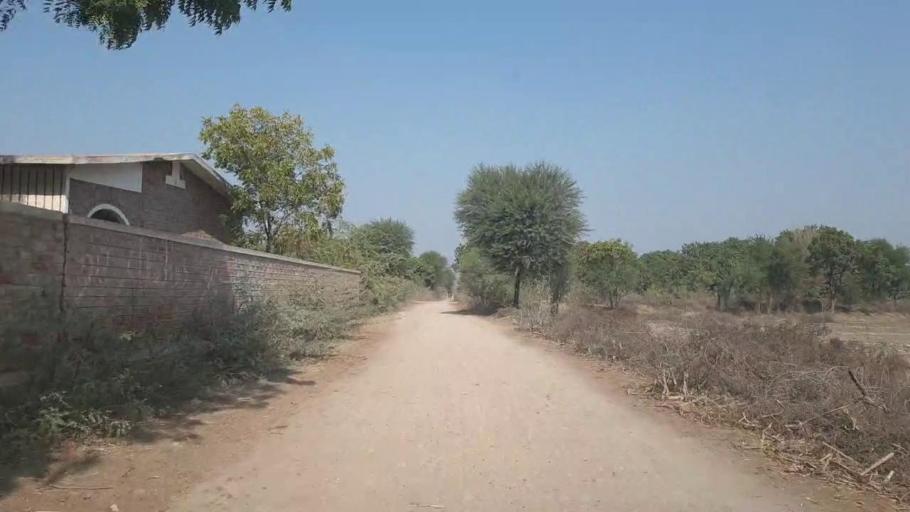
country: PK
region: Sindh
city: Tando Allahyar
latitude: 25.4329
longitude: 68.8359
